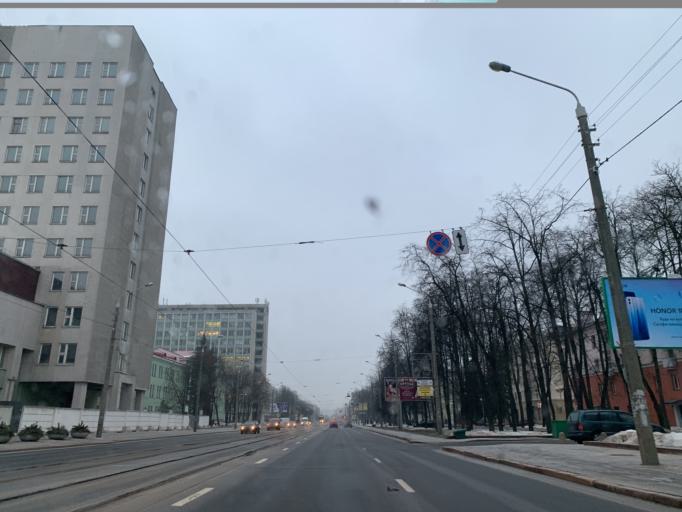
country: BY
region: Minsk
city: Minsk
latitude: 53.9230
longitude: 27.5905
